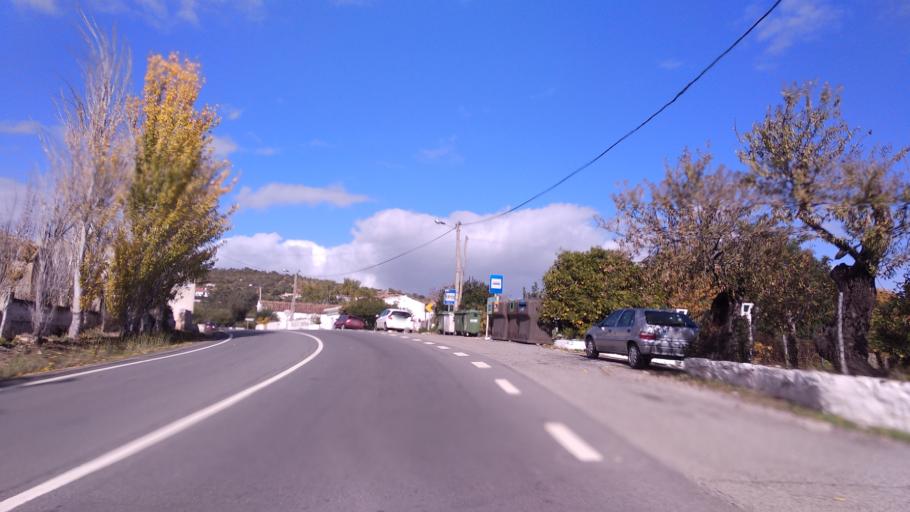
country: PT
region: Faro
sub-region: Sao Bras de Alportel
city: Sao Bras de Alportel
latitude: 37.1287
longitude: -7.8930
